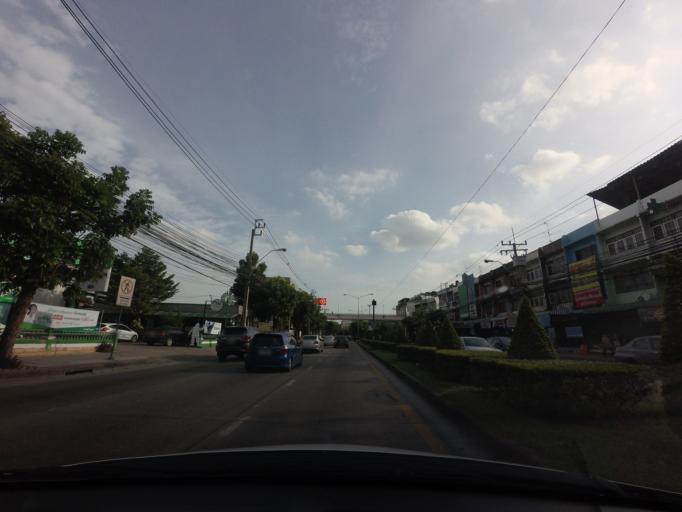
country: TH
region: Bangkok
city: Bueng Kum
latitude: 13.8062
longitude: 100.6484
